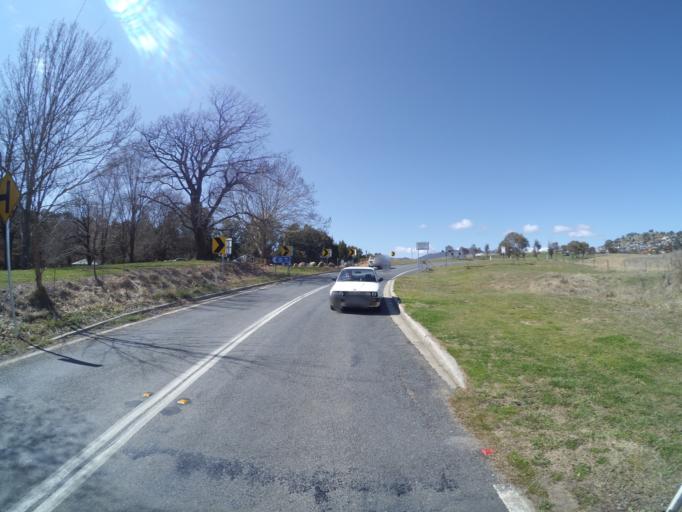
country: AU
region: Australian Capital Territory
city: Macarthur
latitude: -35.4528
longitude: 149.0746
